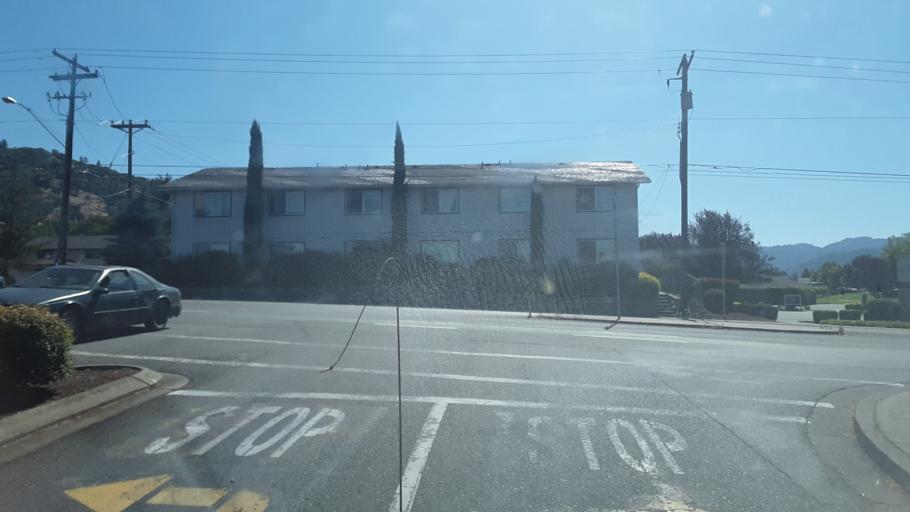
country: US
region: Oregon
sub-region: Josephine County
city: Fruitdale
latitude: 42.4378
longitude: -123.3082
